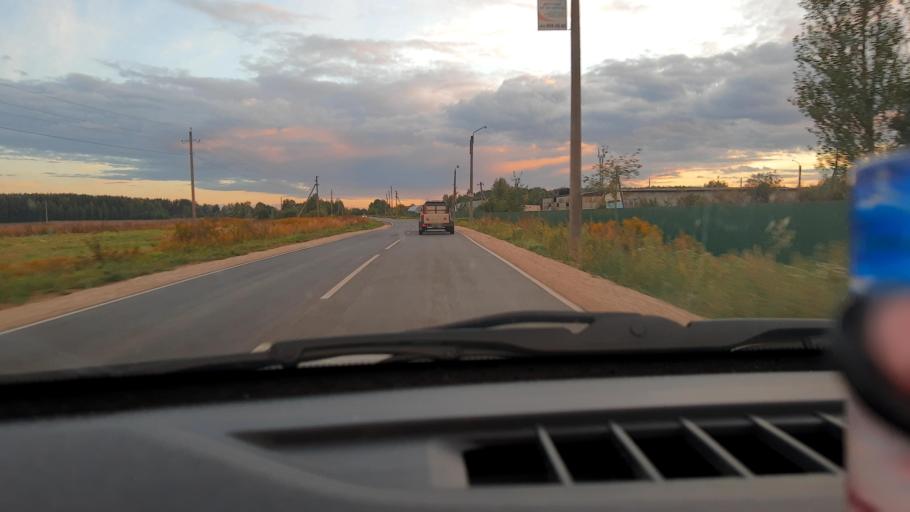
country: RU
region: Nizjnij Novgorod
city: Neklyudovo
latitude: 56.4534
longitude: 43.9041
